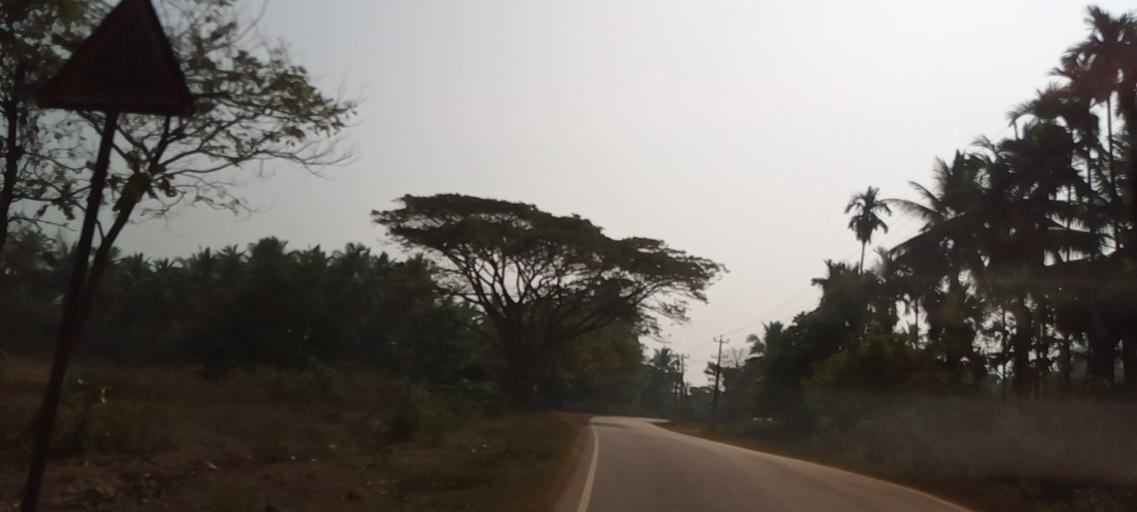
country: IN
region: Karnataka
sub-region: Udupi
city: Coondapoor
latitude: 13.5137
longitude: 74.8046
